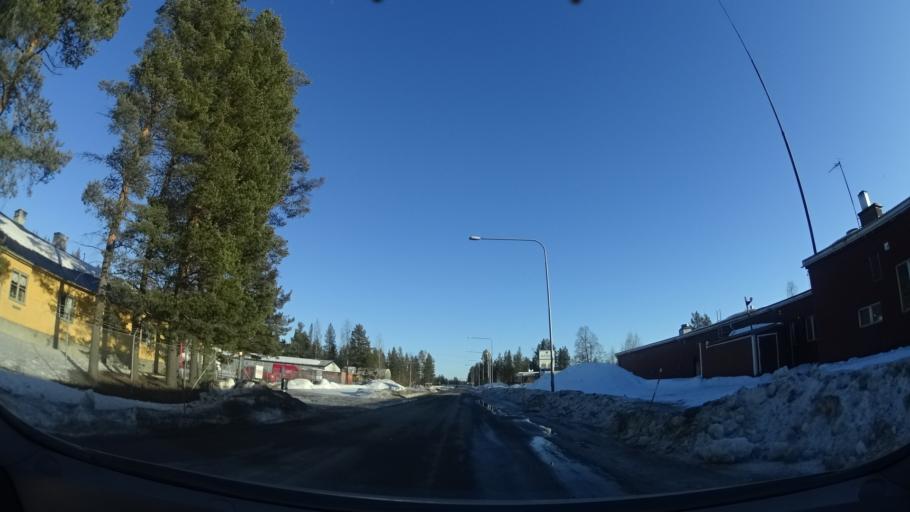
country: SE
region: Vaesterbotten
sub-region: Skelleftea Kommun
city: Langsele
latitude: 65.0552
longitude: 20.0521
